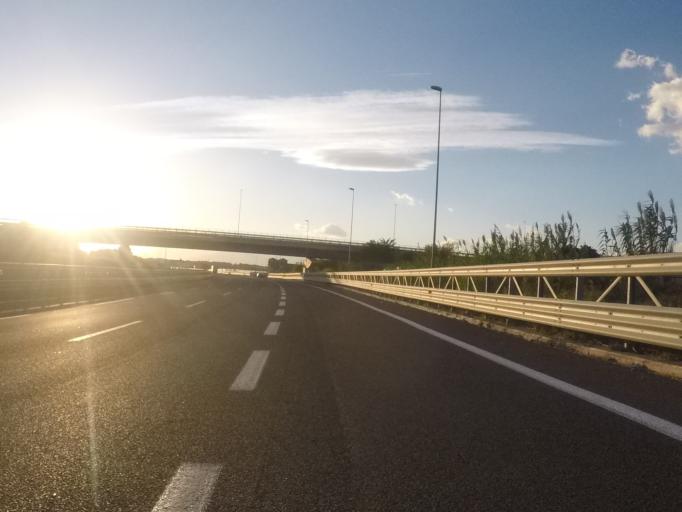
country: IT
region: Campania
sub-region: Provincia di Salerno
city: Battipaglia
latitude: 40.6203
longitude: 14.9750
